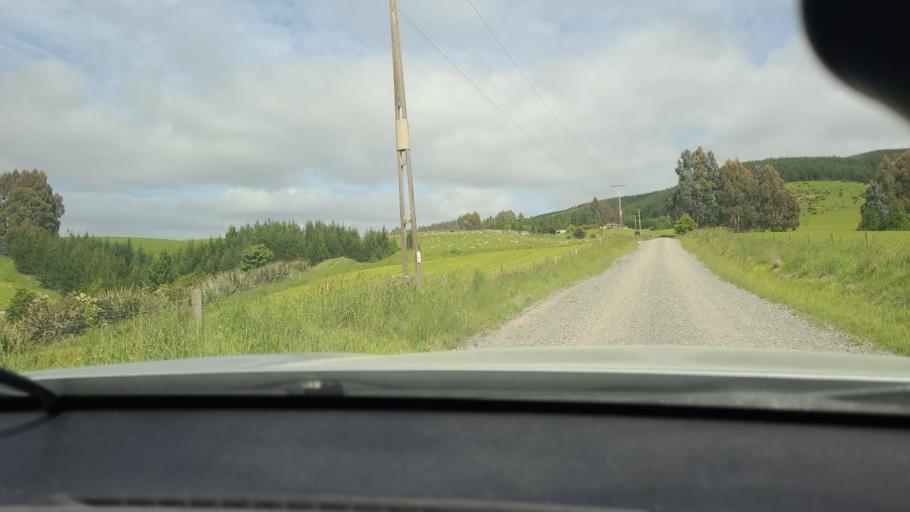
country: NZ
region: Southland
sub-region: Southland District
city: Winton
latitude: -45.9173
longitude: 168.0774
